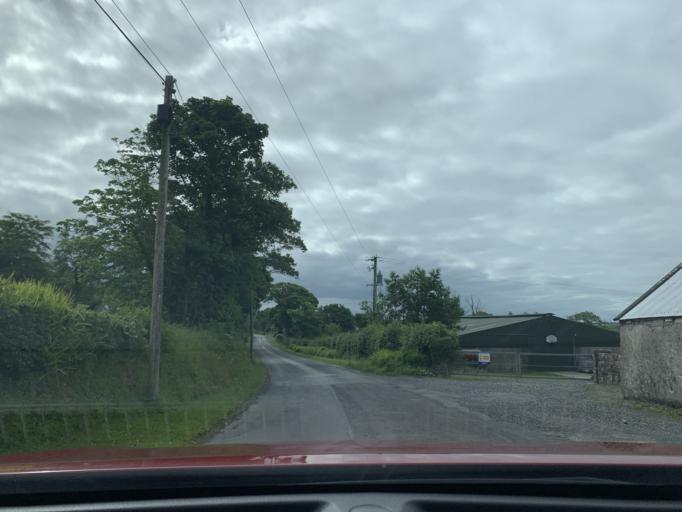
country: IE
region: Connaught
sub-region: Sligo
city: Sligo
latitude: 54.3425
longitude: -8.4859
